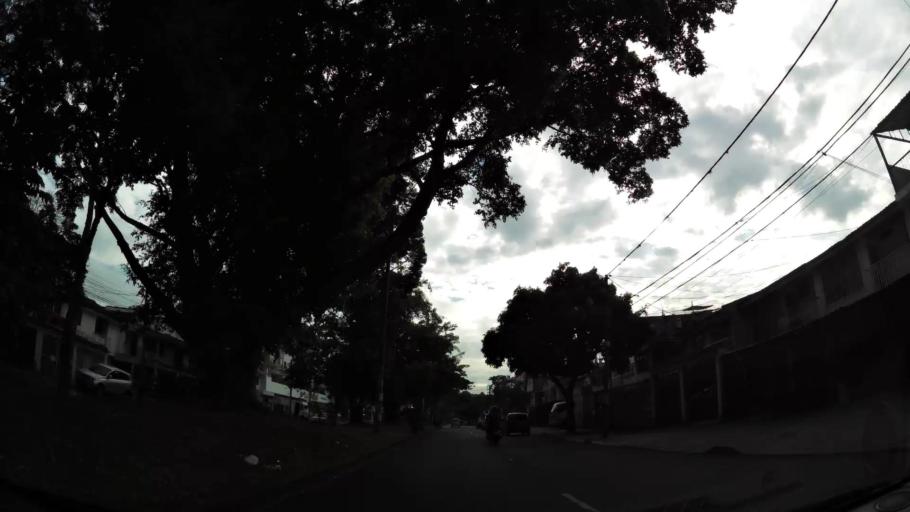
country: CO
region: Valle del Cauca
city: Cali
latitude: 3.4697
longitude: -76.4968
